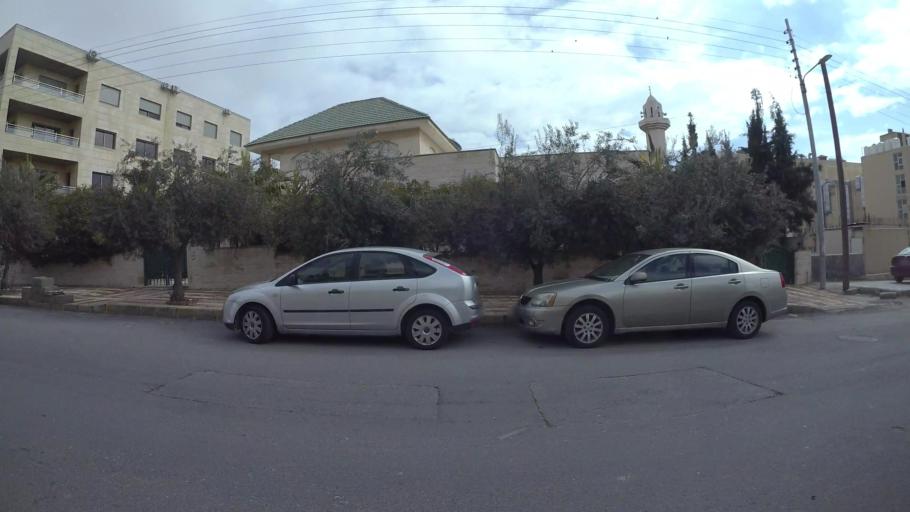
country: JO
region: Amman
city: Al Jubayhah
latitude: 31.9973
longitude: 35.8360
